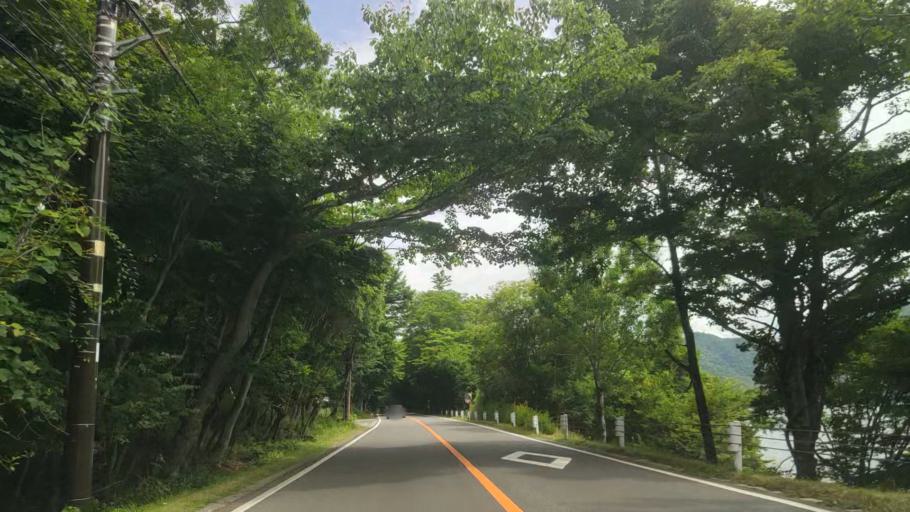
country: JP
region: Tochigi
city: Nikko
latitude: 36.7461
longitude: 139.4703
